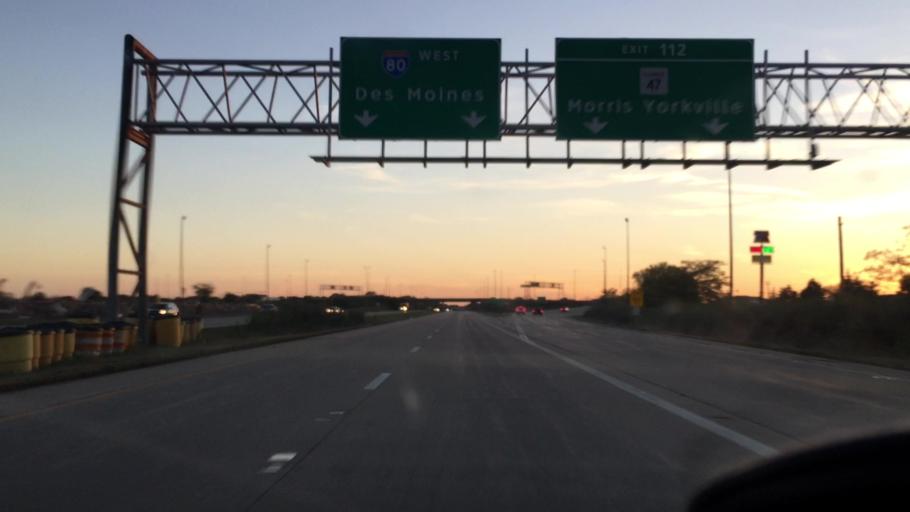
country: US
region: Illinois
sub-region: Grundy County
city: Morris
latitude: 41.3918
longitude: -88.4171
